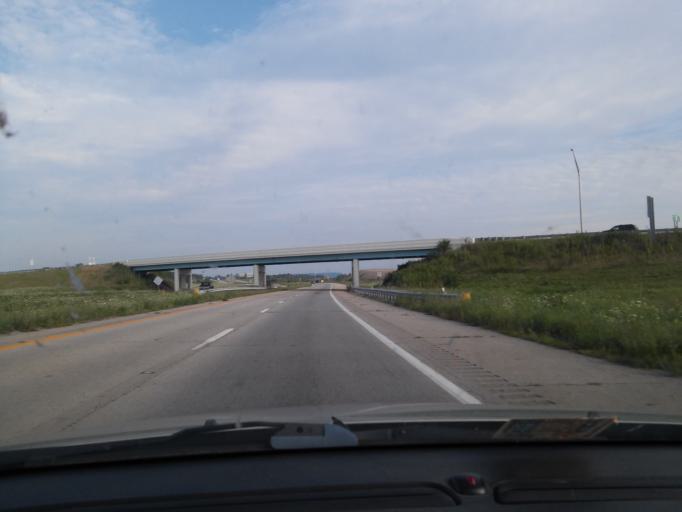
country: US
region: Ohio
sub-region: Ross County
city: Chillicothe
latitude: 39.3000
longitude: -82.9117
